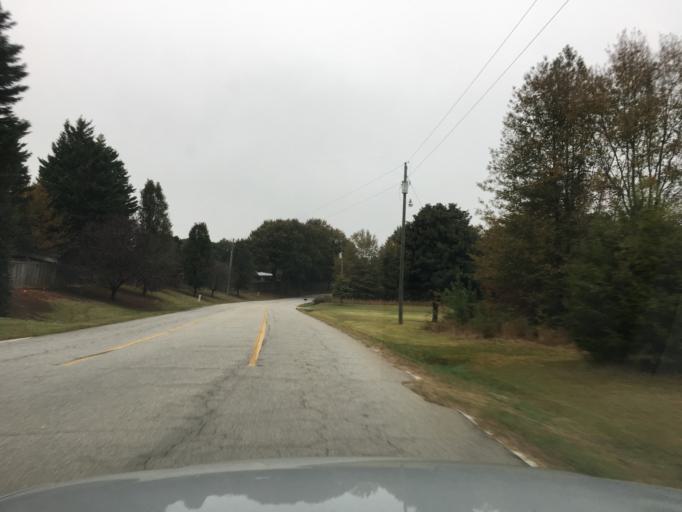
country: US
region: South Carolina
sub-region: Greenville County
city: Five Forks
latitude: 34.8268
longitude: -82.2702
